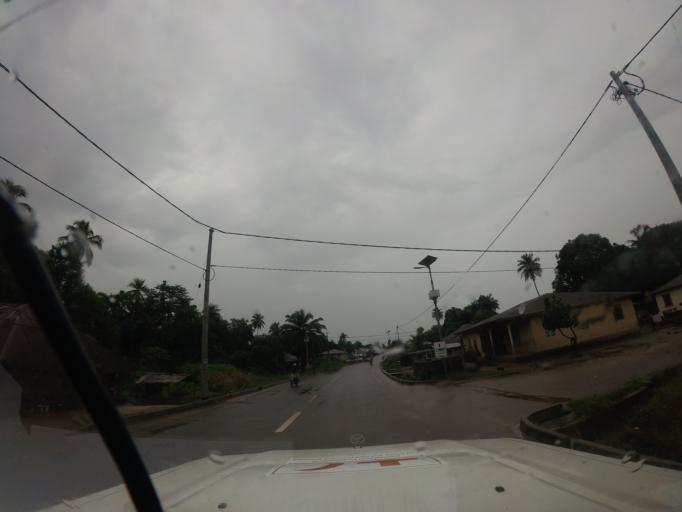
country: SL
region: Northern Province
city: Makeni
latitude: 8.8822
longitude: -12.0477
